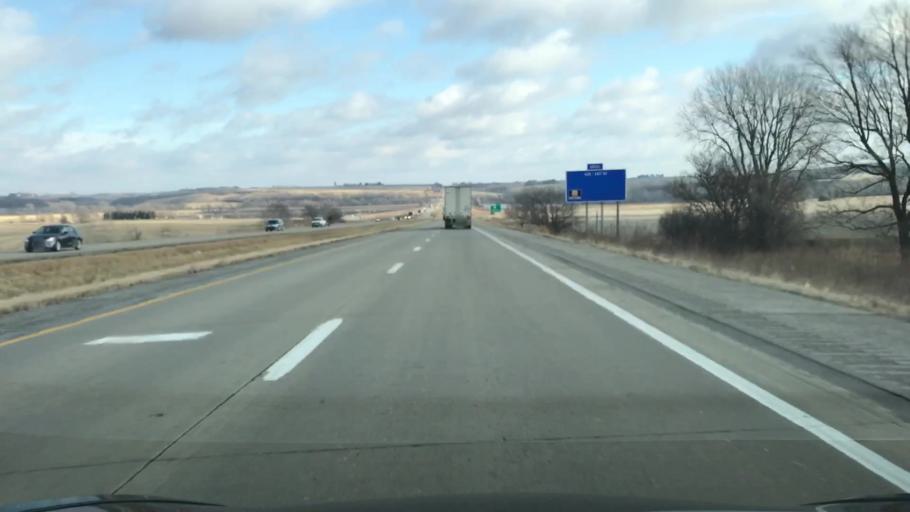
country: US
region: Iowa
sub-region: Cass County
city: Atlantic
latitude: 41.4959
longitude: -94.9568
